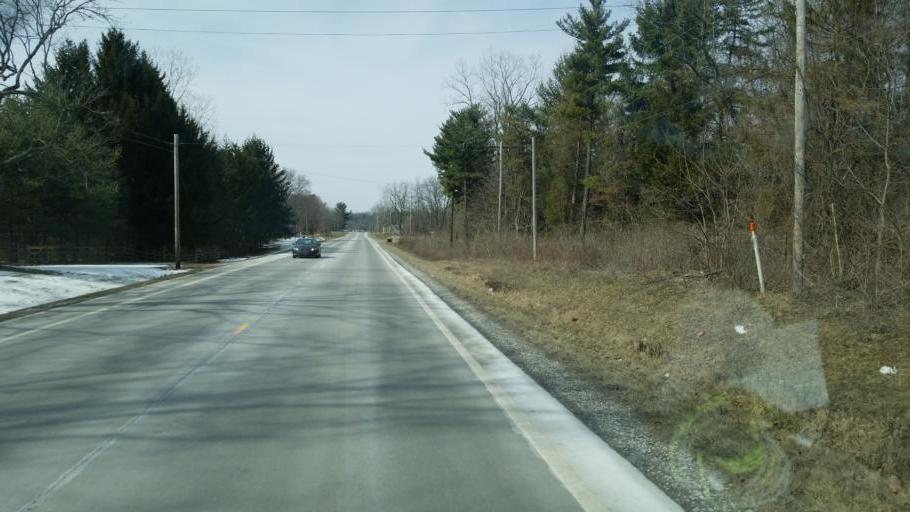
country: US
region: Ohio
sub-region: Delaware County
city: Sunbury
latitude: 40.2622
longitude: -82.8924
